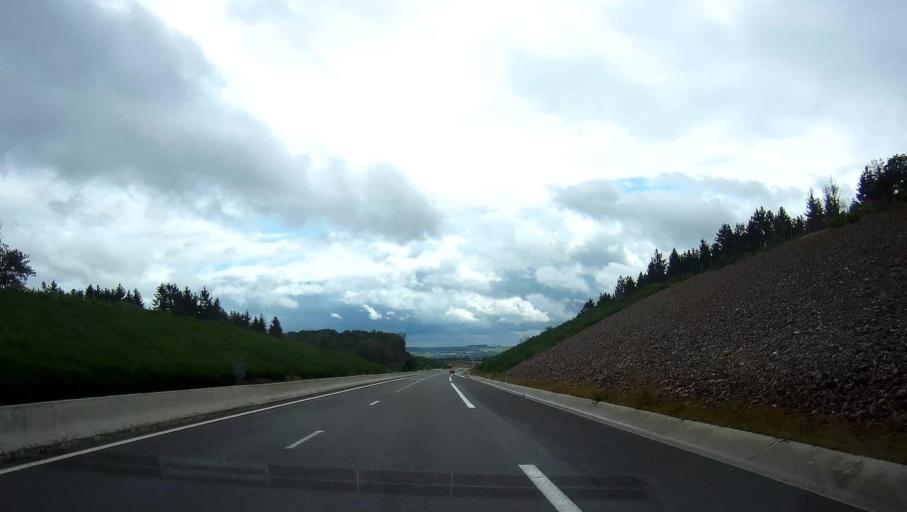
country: FR
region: Champagne-Ardenne
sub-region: Departement des Ardennes
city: Rimogne
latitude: 49.8522
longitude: 4.5129
